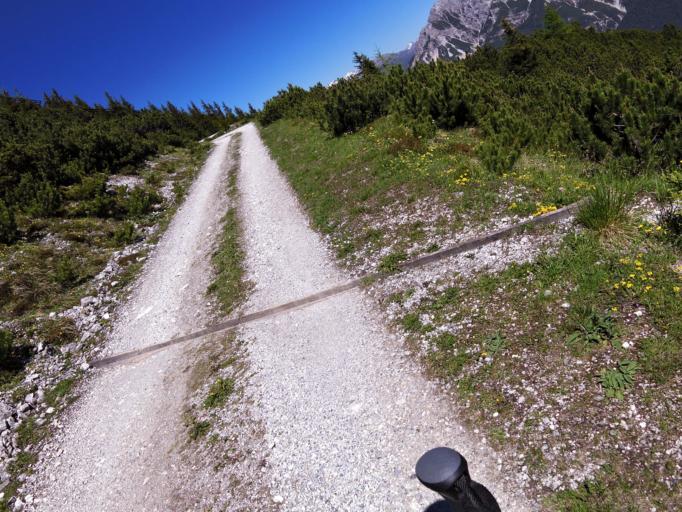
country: AT
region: Tyrol
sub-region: Politischer Bezirk Innsbruck Land
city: Neustift im Stubaital
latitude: 47.1270
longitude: 11.2940
